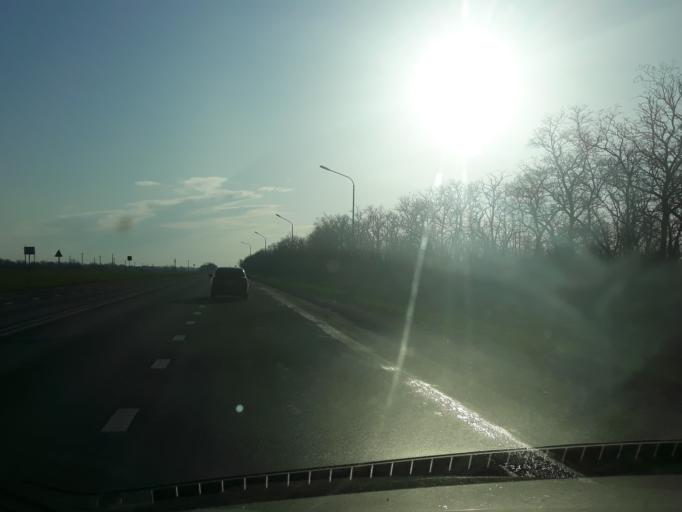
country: RU
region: Rostov
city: Novobessergenovka
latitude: 47.1885
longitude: 38.6211
